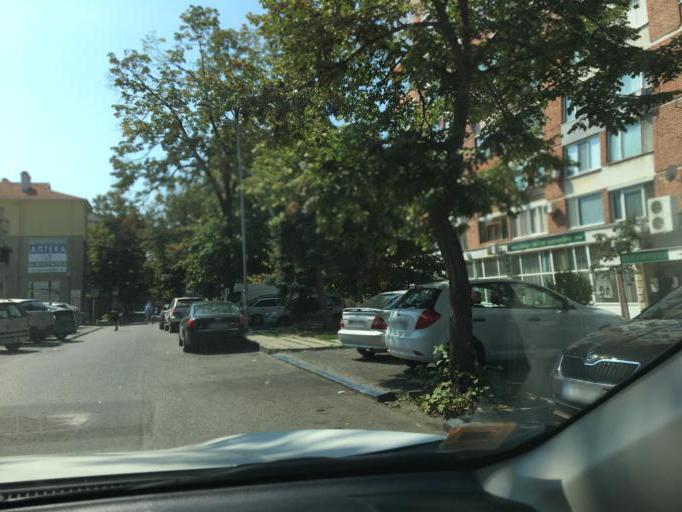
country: BG
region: Burgas
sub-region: Obshtina Burgas
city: Burgas
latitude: 42.4934
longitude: 27.4639
